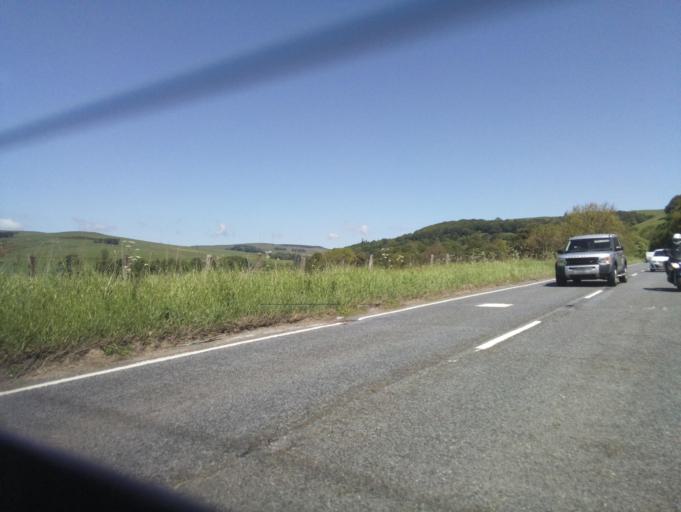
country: GB
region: Scotland
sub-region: The Scottish Borders
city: Galashiels
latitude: 55.6721
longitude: -2.8705
